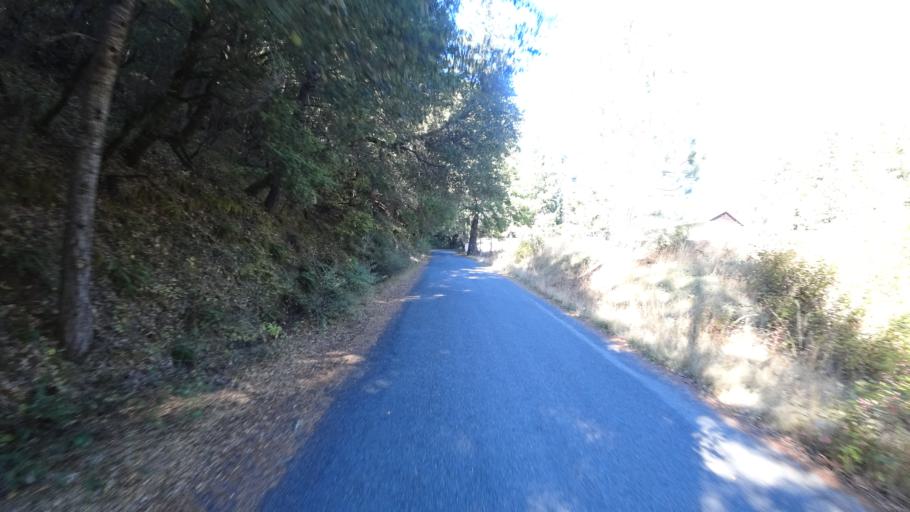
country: US
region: California
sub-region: Siskiyou County
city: Happy Camp
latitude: 41.3819
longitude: -123.4936
